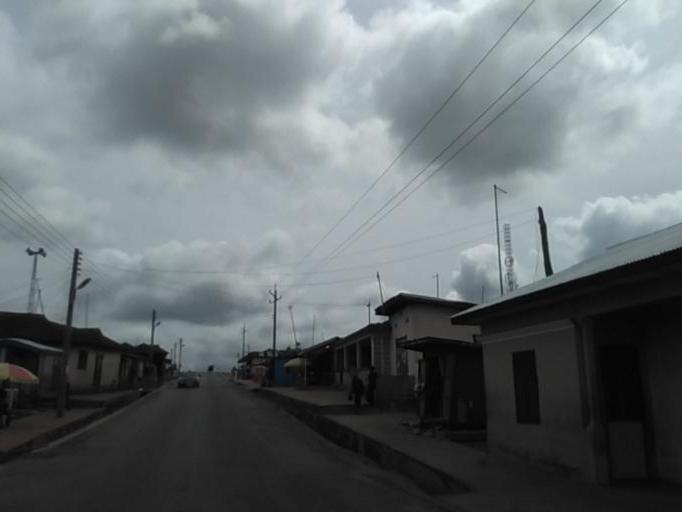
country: GH
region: Ashanti
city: Mamponteng
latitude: 6.7503
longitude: -1.4562
